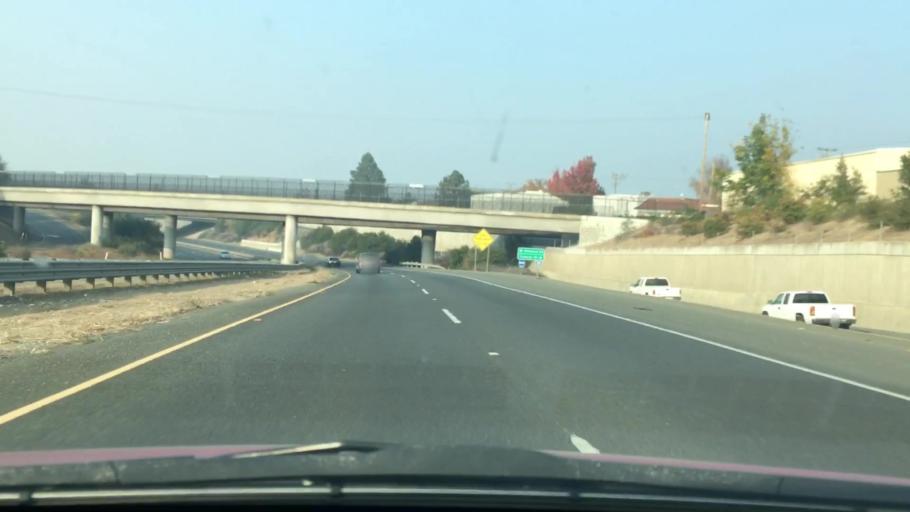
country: US
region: California
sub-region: Napa County
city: Napa
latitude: 38.3180
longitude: -122.3075
